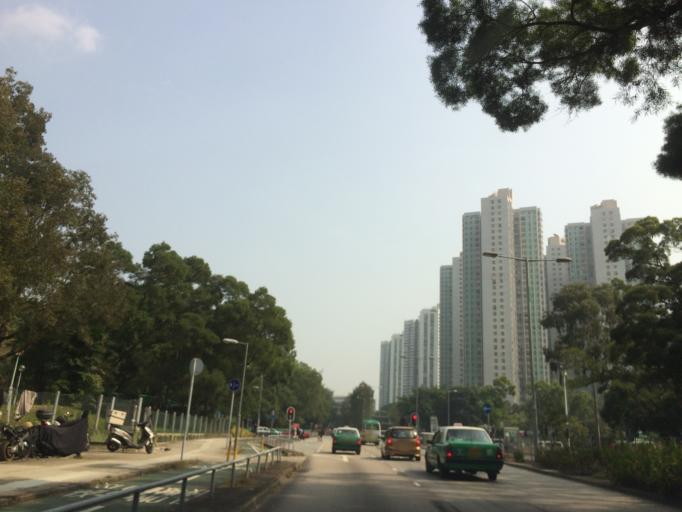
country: HK
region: Tai Po
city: Tai Po
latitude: 22.4562
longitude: 114.1710
